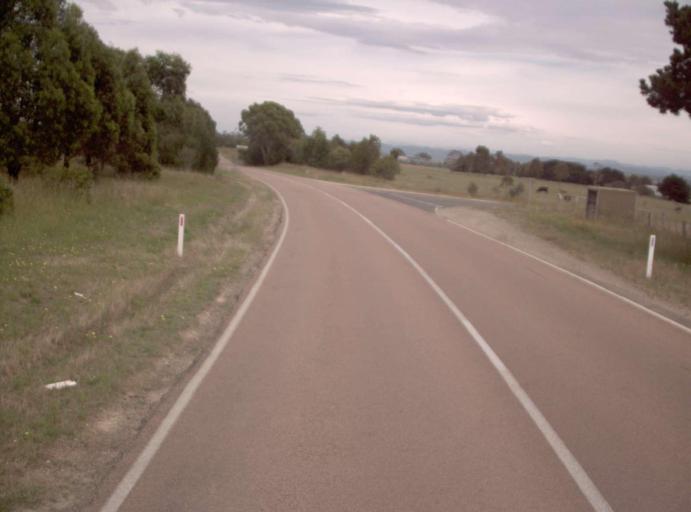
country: AU
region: Victoria
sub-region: East Gippsland
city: Bairnsdale
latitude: -37.8310
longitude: 147.5526
